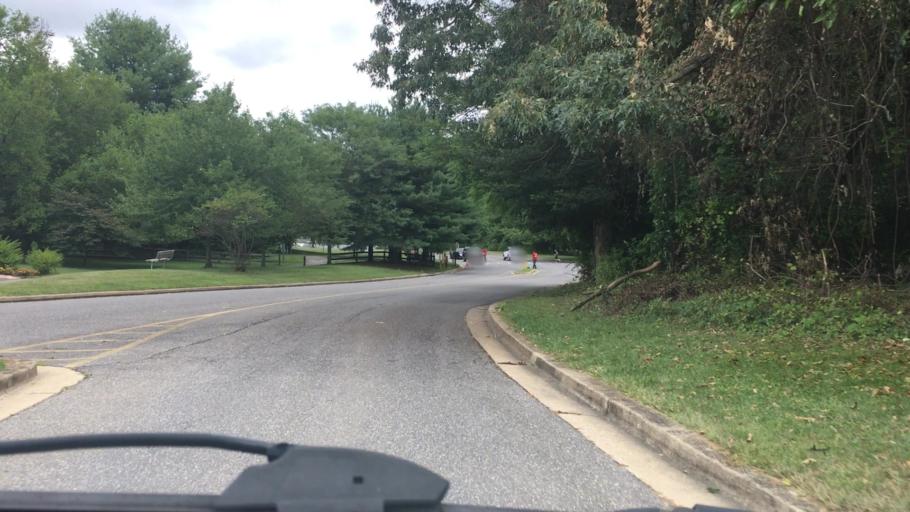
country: US
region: Maryland
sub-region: Anne Arundel County
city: Pasadena
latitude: 39.0998
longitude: -76.5792
